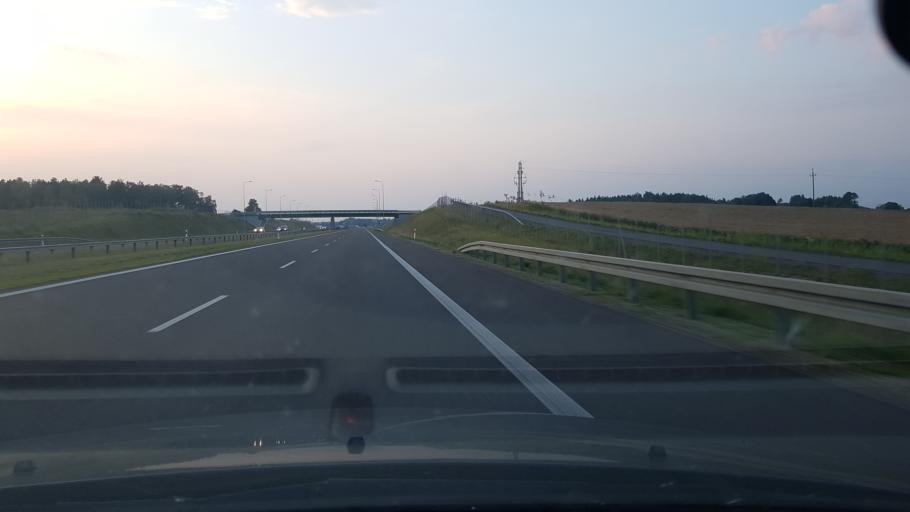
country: PL
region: Warmian-Masurian Voivodeship
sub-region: Powiat nidzicki
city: Nidzica
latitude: 53.2928
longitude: 20.4381
